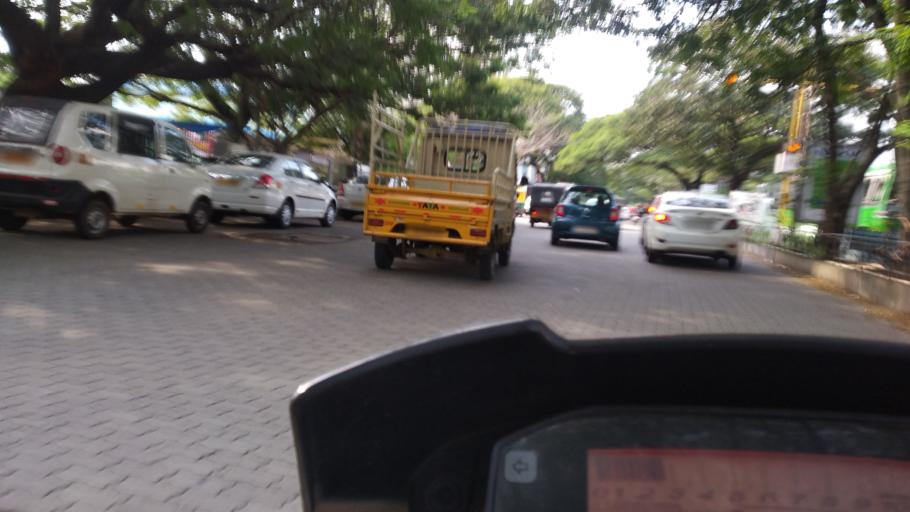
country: IN
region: Kerala
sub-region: Ernakulam
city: Cochin
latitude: 9.9822
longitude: 76.2748
